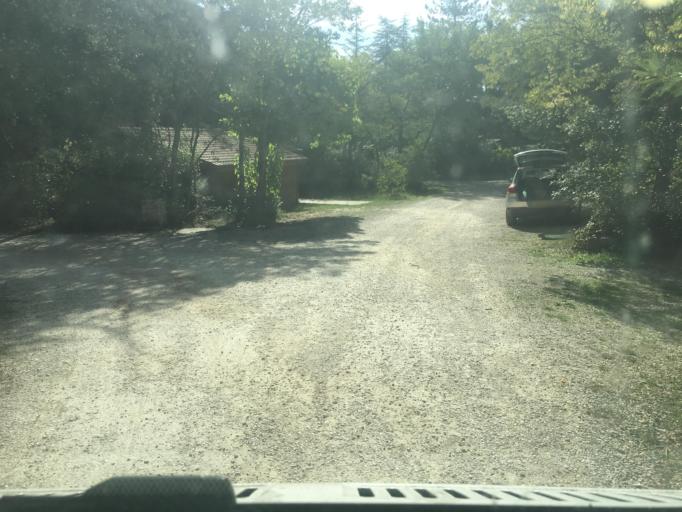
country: FR
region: Languedoc-Roussillon
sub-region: Departement du Gard
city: Montaren-et-Saint-Mediers
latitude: 43.9984
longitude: 4.3844
